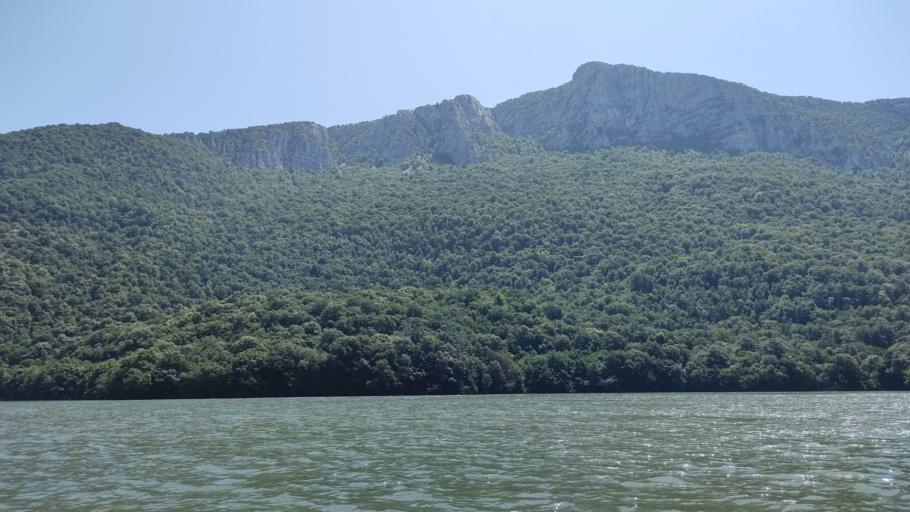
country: RO
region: Mehedinti
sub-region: Comuna Dubova
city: Dubova
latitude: 44.5996
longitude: 22.2652
